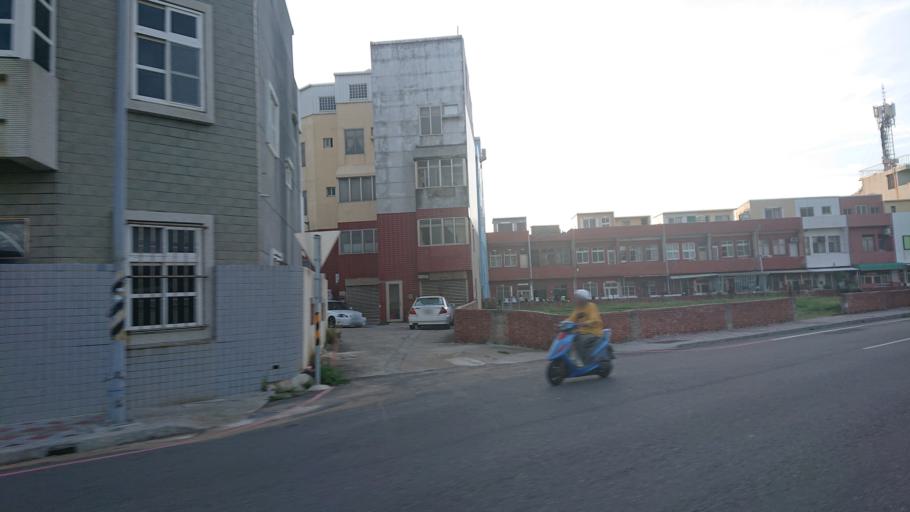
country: TW
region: Taiwan
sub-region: Penghu
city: Ma-kung
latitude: 23.5710
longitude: 119.5817
